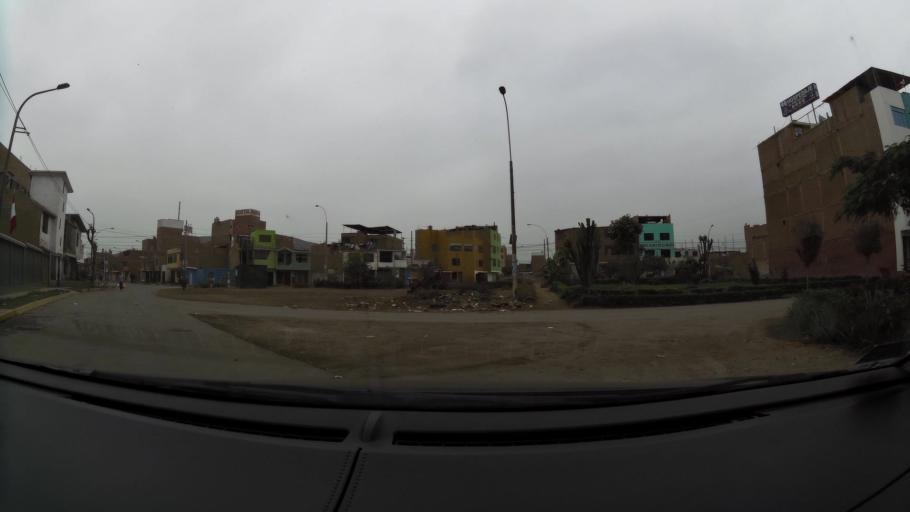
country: PE
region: Lima
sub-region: Lima
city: Independencia
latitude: -11.9478
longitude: -77.0873
